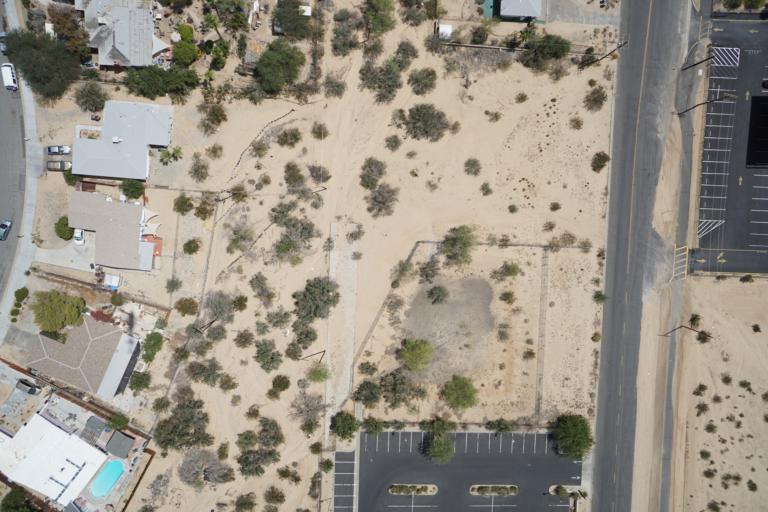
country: US
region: California
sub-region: San Bernardino County
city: Twentynine Palms
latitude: 34.1433
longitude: -116.0677
